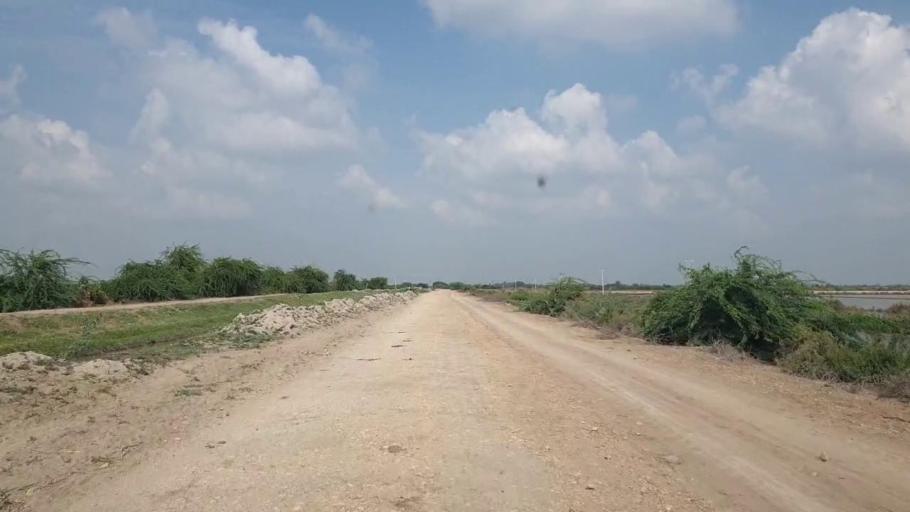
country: PK
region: Sindh
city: Badin
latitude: 24.5043
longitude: 68.6558
